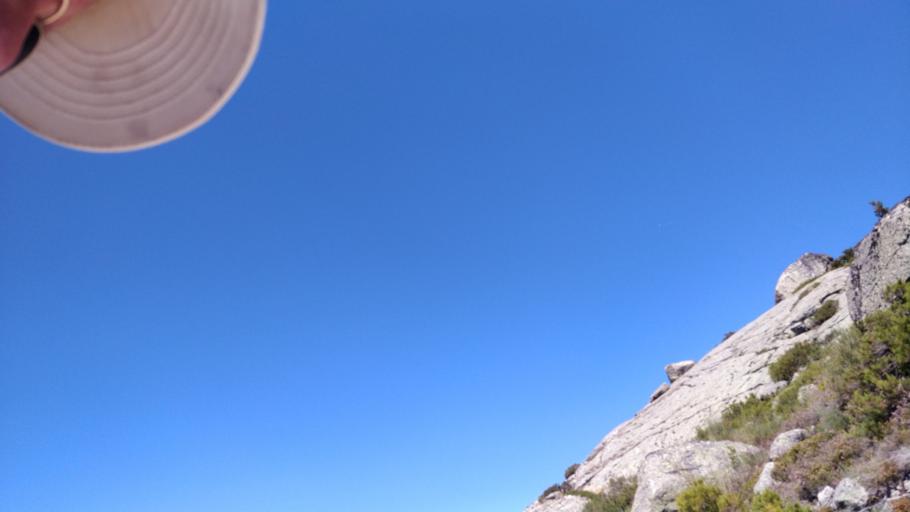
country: PT
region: Guarda
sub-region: Seia
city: Seia
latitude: 40.3626
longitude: -7.6278
